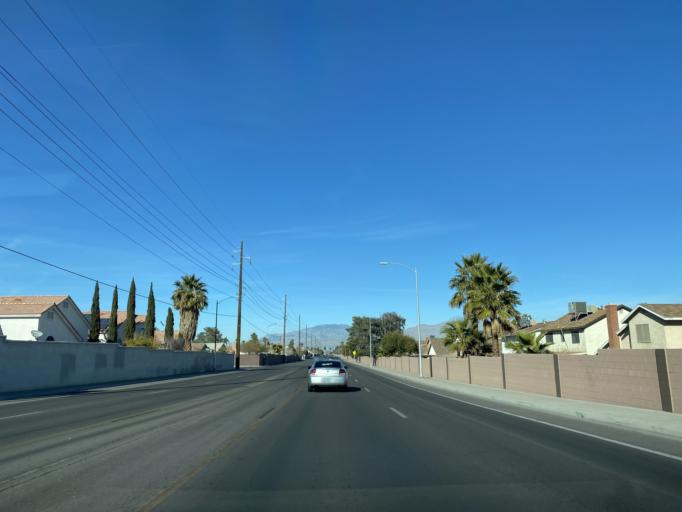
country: US
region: Nevada
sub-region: Clark County
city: Spring Valley
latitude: 36.1860
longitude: -115.2512
